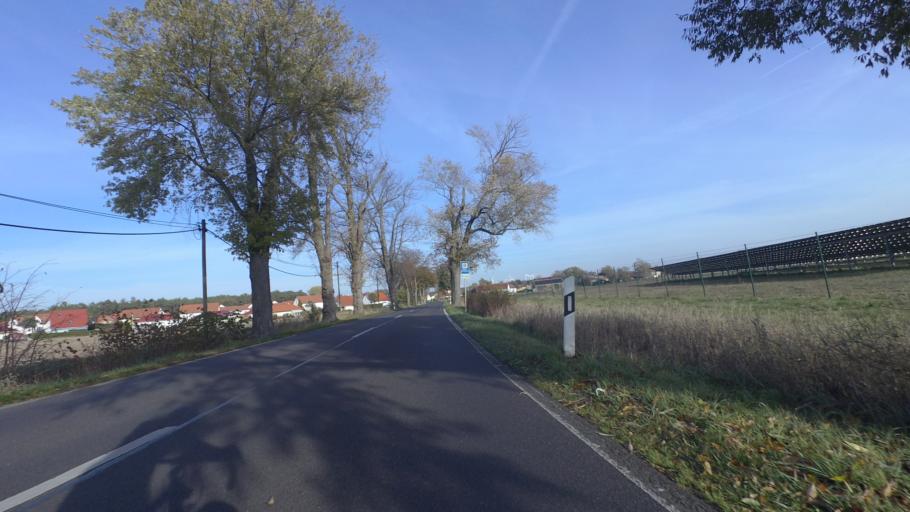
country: DE
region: Brandenburg
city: Trebbin
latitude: 52.1919
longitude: 13.2374
